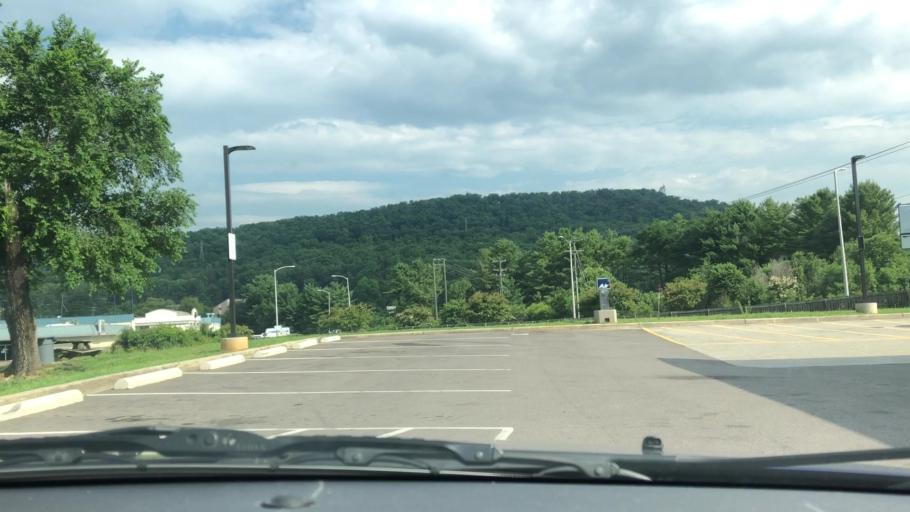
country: US
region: Virginia
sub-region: Roanoke County
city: Hollins
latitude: 37.3588
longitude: -79.9579
